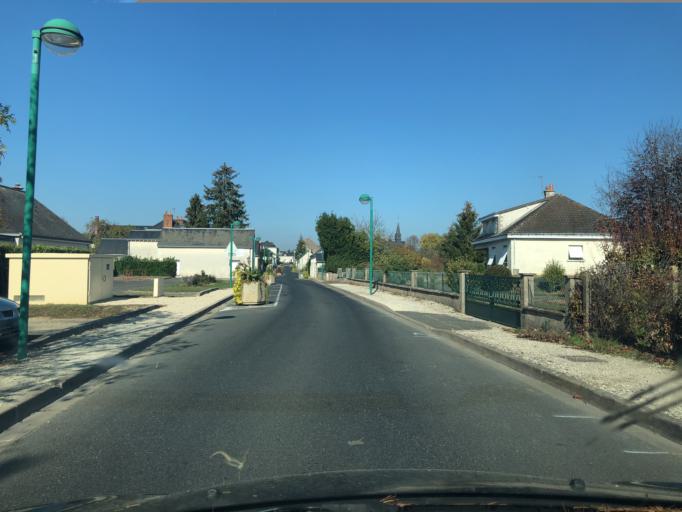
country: FR
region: Centre
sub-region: Departement d'Indre-et-Loire
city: Rouziers-de-Touraine
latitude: 47.5144
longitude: 0.6491
